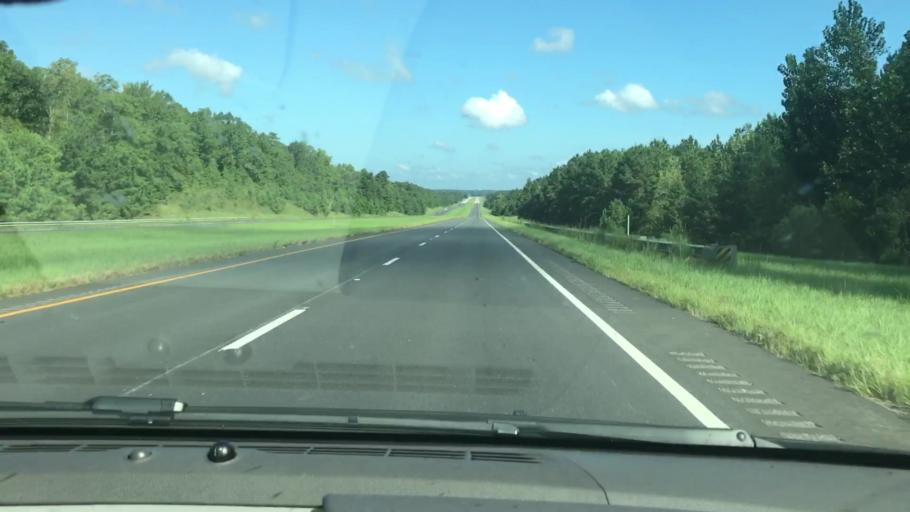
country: US
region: Alabama
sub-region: Barbour County
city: Eufaula
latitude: 32.0488
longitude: -85.1323
